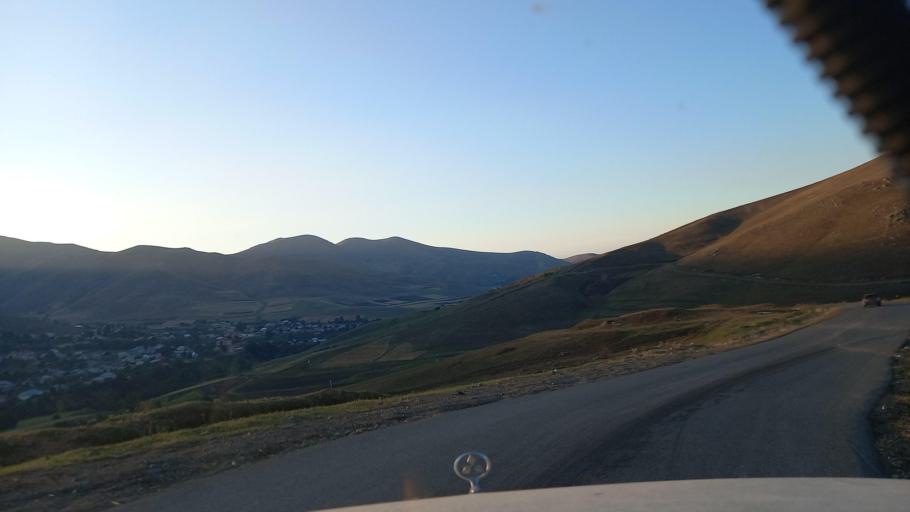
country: AZ
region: Gadabay Rayon
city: Ariqdam
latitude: 40.6824
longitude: 45.7722
